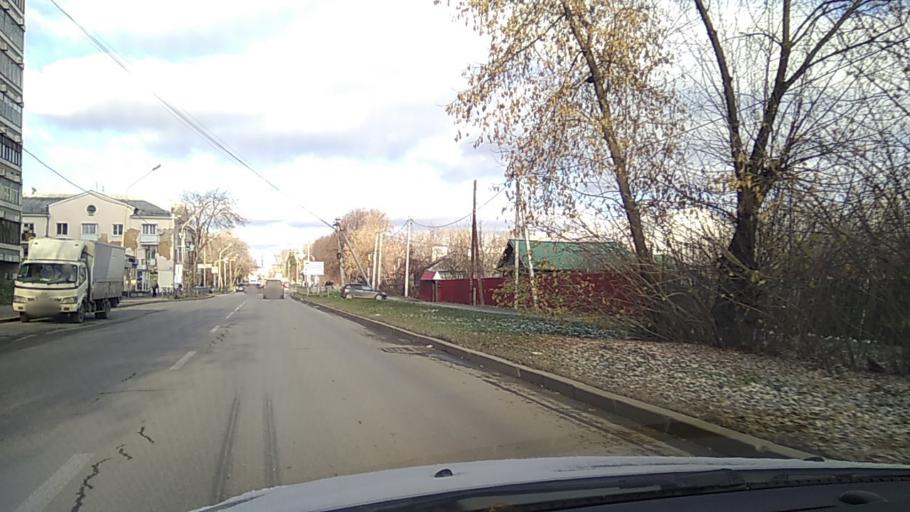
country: RU
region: Sverdlovsk
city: Sovkhoznyy
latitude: 56.7525
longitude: 60.6222
